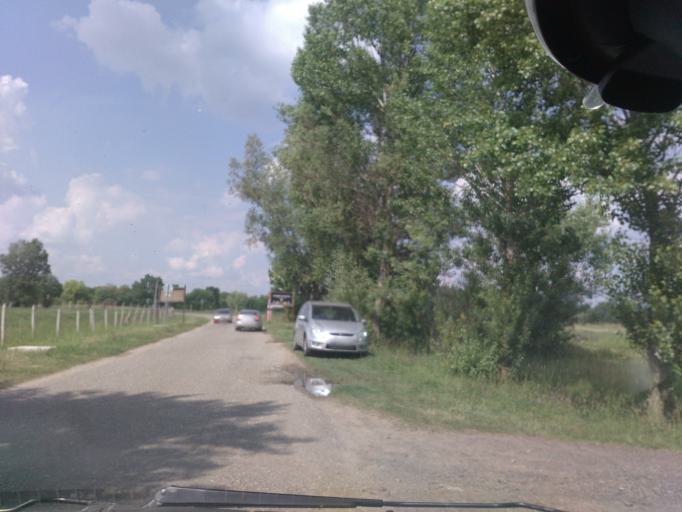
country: HU
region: Pest
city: Veresegyhaz
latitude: 47.6367
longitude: 19.2606
